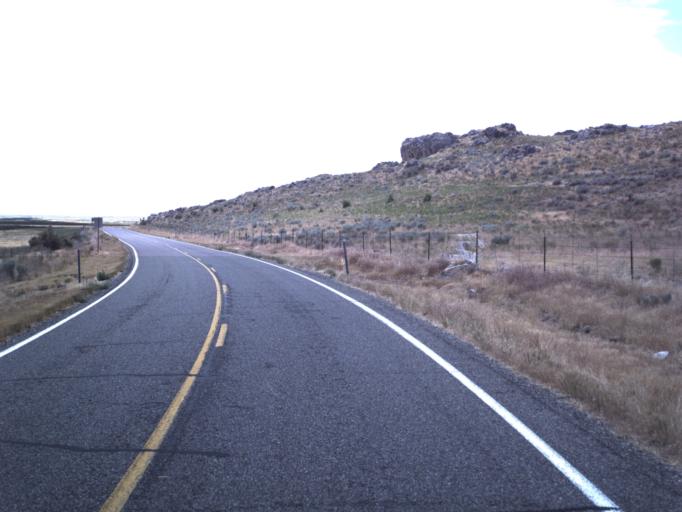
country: US
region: Utah
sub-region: Box Elder County
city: Tremonton
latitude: 41.6167
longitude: -112.3672
